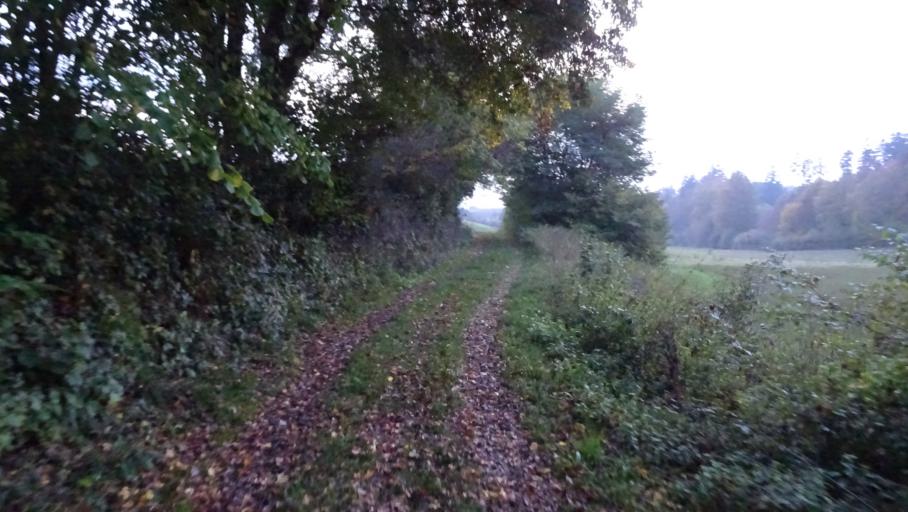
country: DE
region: Baden-Wuerttemberg
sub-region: Karlsruhe Region
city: Obrigheim
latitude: 49.3786
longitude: 9.0885
